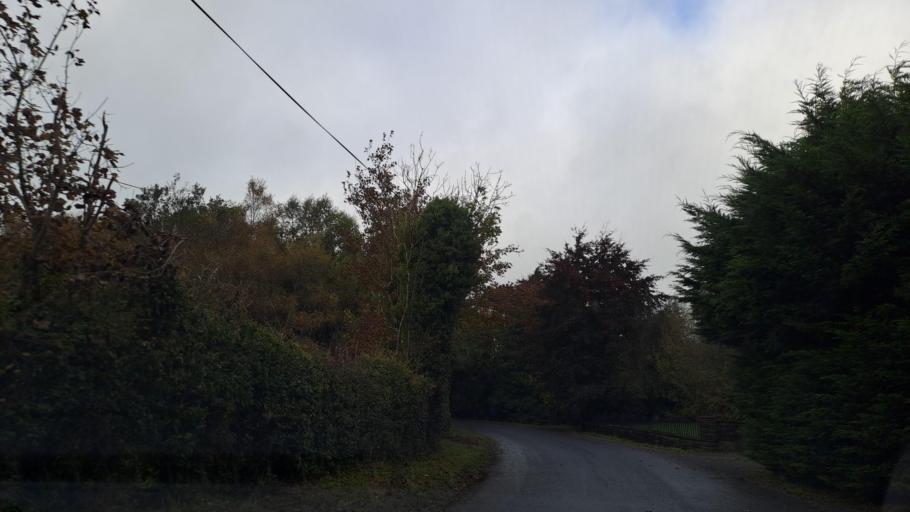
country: IE
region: Ulster
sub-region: An Cabhan
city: Bailieborough
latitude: 53.9908
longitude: -6.9903
